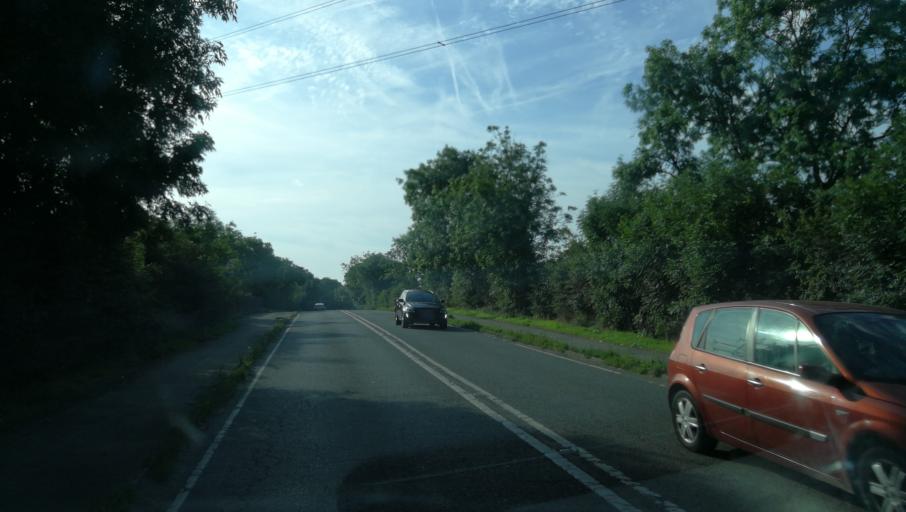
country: GB
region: England
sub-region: Oxfordshire
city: Yarnton
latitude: 51.8054
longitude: -1.2987
